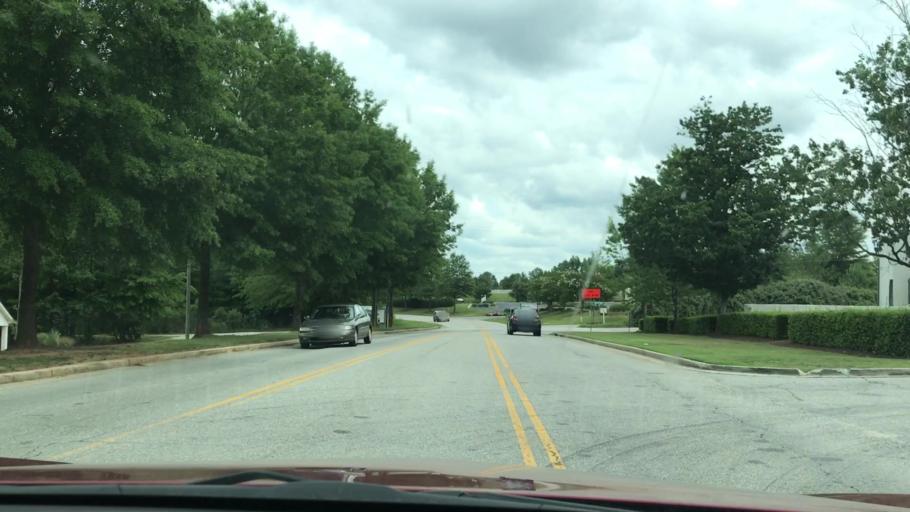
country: US
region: South Carolina
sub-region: Lexington County
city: Irmo
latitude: 34.0920
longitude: -81.1709
